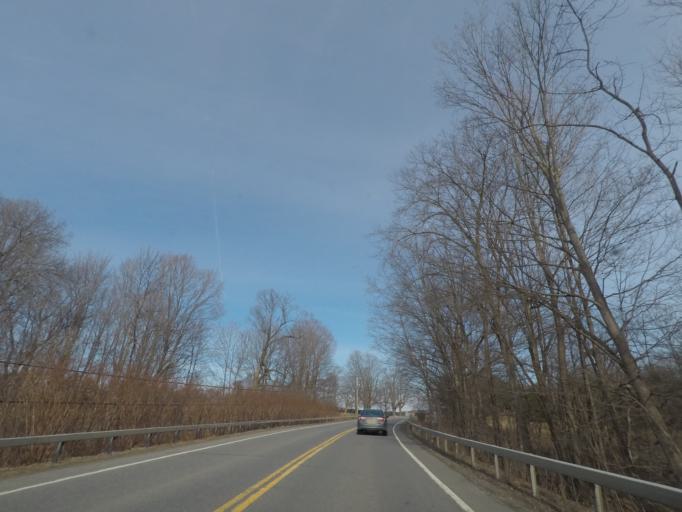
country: US
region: New York
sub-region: Columbia County
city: Niverville
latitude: 42.4622
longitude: -73.6426
